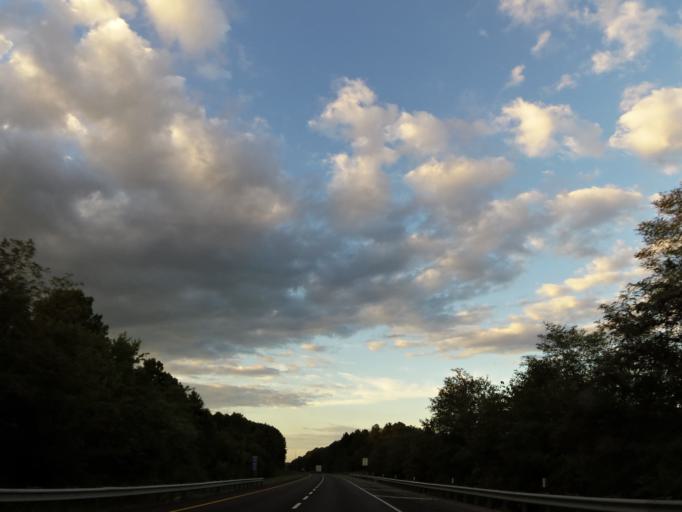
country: US
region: Tennessee
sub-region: Bradley County
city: Hopewell
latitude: 35.2754
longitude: -84.8213
